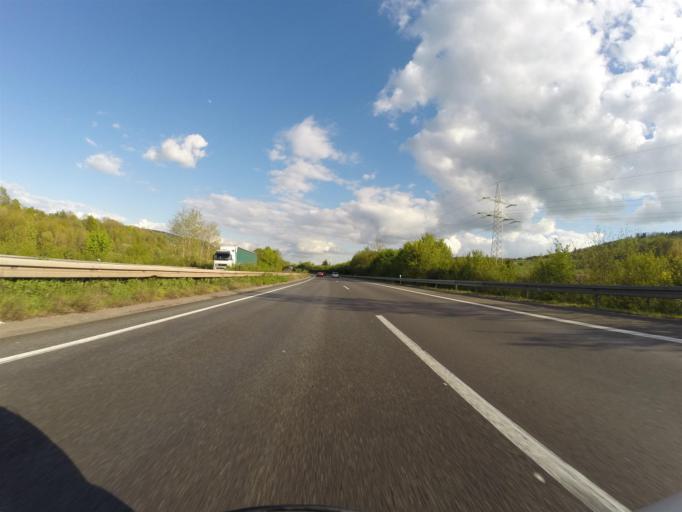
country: DE
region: Saarland
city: Merzig
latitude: 49.4121
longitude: 6.6408
